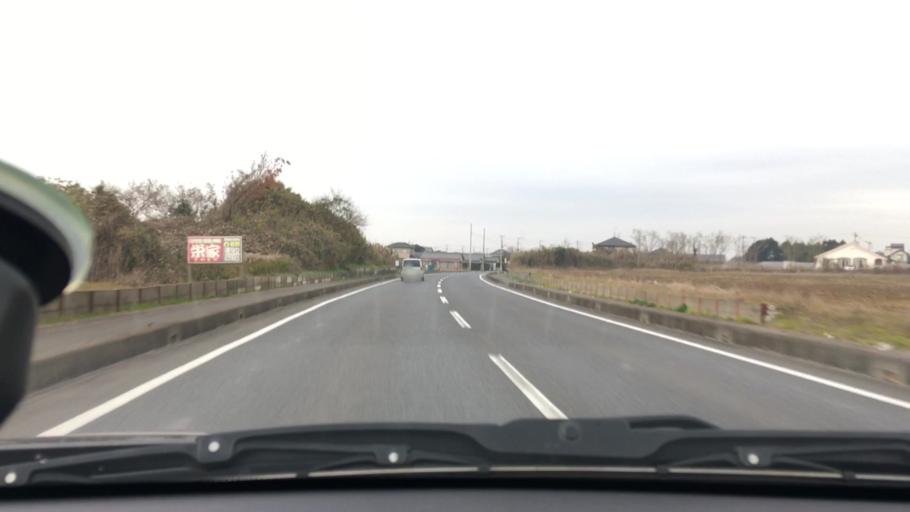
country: JP
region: Chiba
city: Omigawa
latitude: 35.8740
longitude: 140.6362
